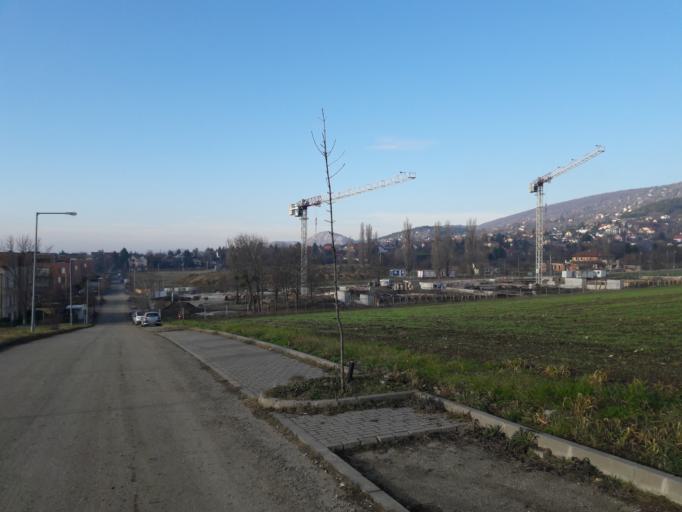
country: HU
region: Pest
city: Budaors
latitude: 47.4665
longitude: 18.9860
